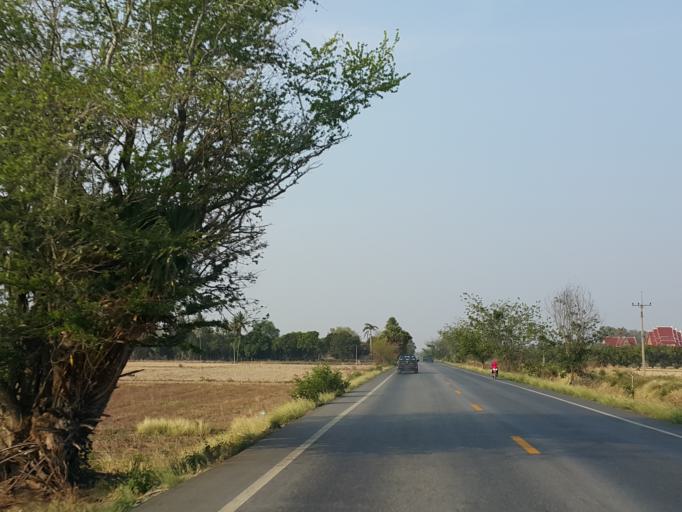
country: TH
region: Chai Nat
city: Sankhaburi
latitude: 14.9840
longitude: 100.1086
